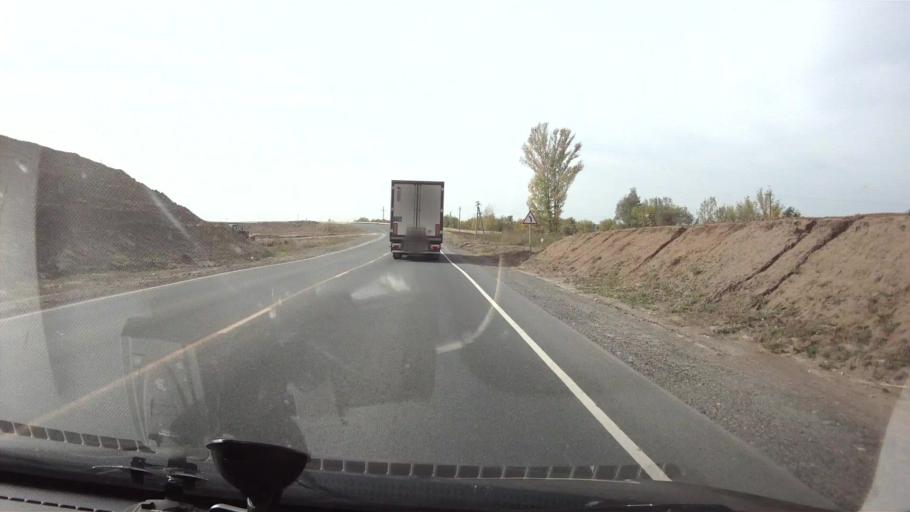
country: RU
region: Saratov
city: Sennoy
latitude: 52.1605
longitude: 47.0558
